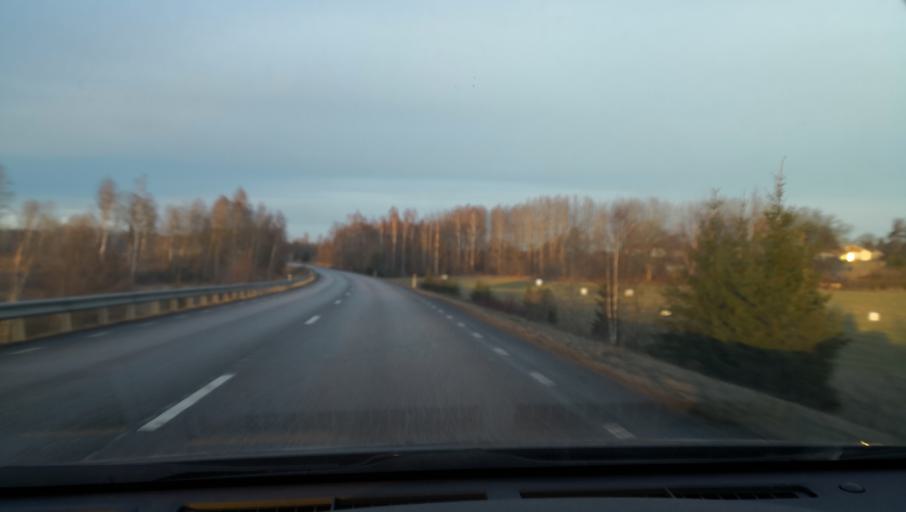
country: SE
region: OErebro
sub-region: Lekebergs Kommun
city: Fjugesta
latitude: 59.1755
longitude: 14.8548
